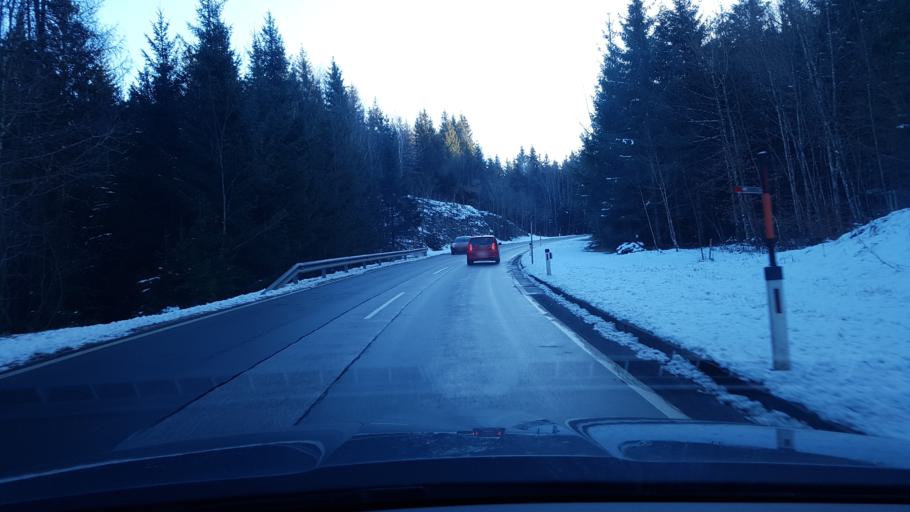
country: AT
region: Salzburg
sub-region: Politischer Bezirk Hallein
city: Adnet
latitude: 47.6646
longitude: 13.1623
